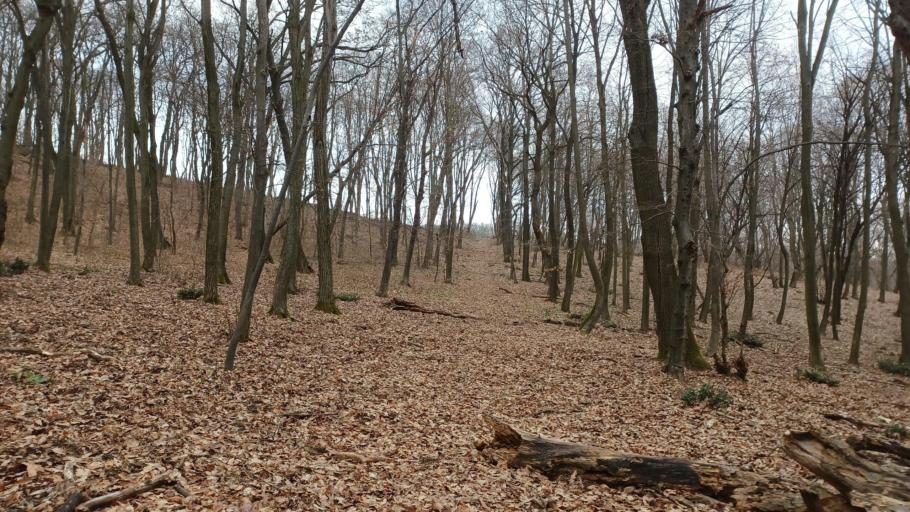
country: HU
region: Tolna
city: Szentgalpuszta
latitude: 46.3000
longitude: 18.6326
